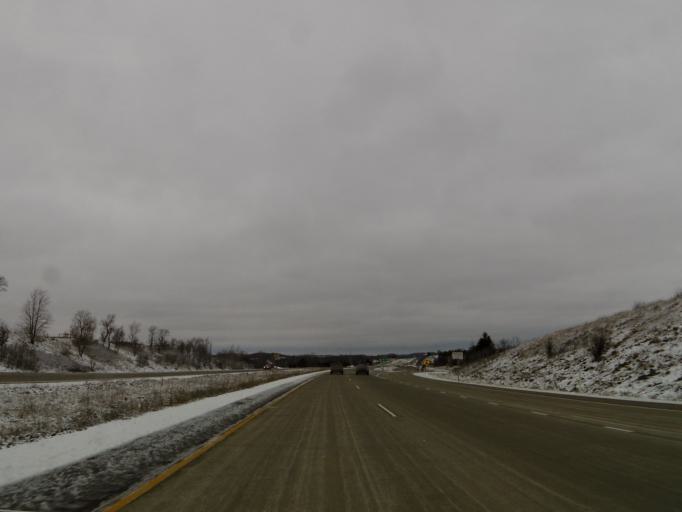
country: US
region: Wisconsin
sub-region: Trempealeau County
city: Osseo
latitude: 44.6393
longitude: -91.3033
